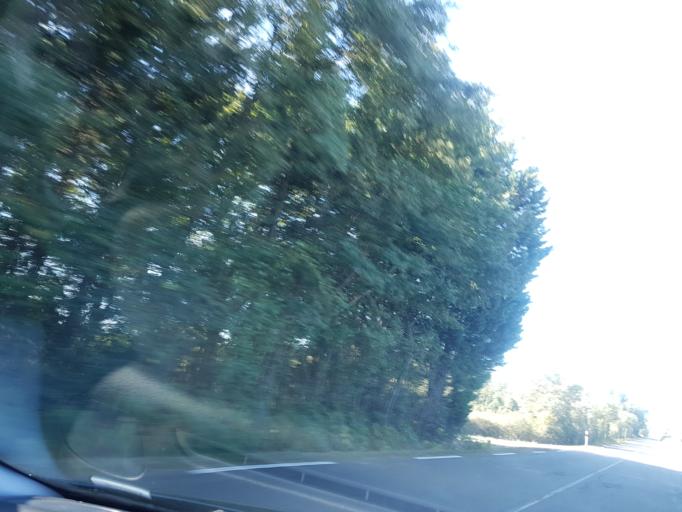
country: FR
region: Pays de la Loire
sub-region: Departement de la Loire-Atlantique
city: Casson
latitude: 47.4284
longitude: -1.5717
